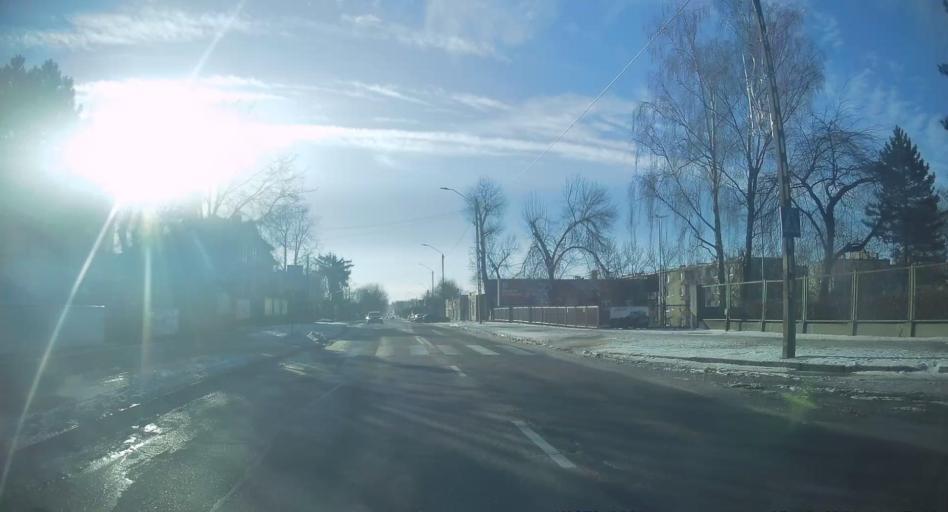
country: PL
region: Lodz Voivodeship
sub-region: Powiat rawski
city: Rawa Mazowiecka
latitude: 51.7601
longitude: 20.2459
